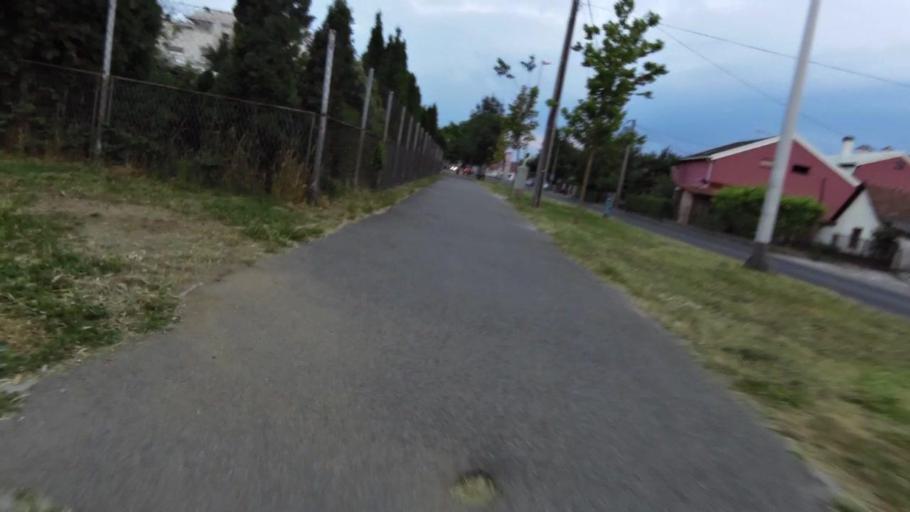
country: HR
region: Grad Zagreb
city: Dubrava
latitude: 45.8306
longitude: 16.0635
